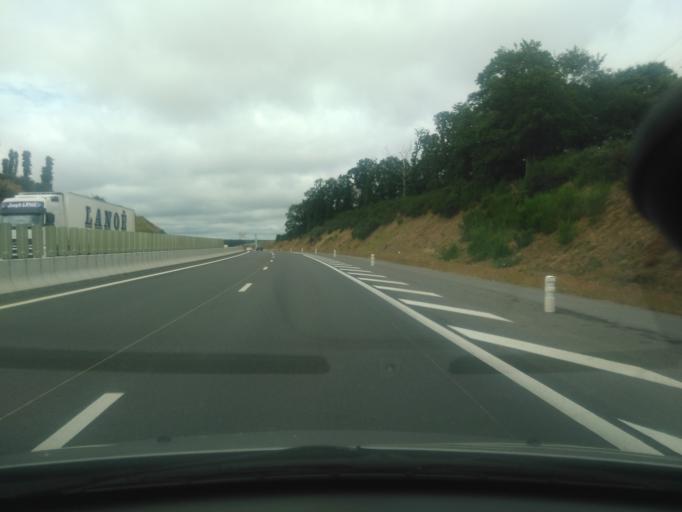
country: FR
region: Brittany
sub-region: Departement des Cotes-d'Armor
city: Pledran
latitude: 48.4759
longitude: -2.7426
